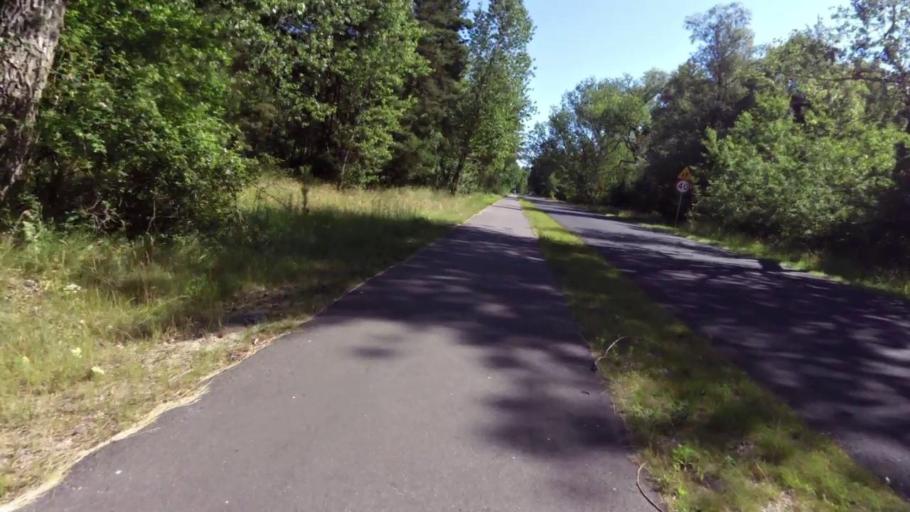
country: PL
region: West Pomeranian Voivodeship
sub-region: Koszalin
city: Koszalin
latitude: 54.2925
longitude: 16.1647
